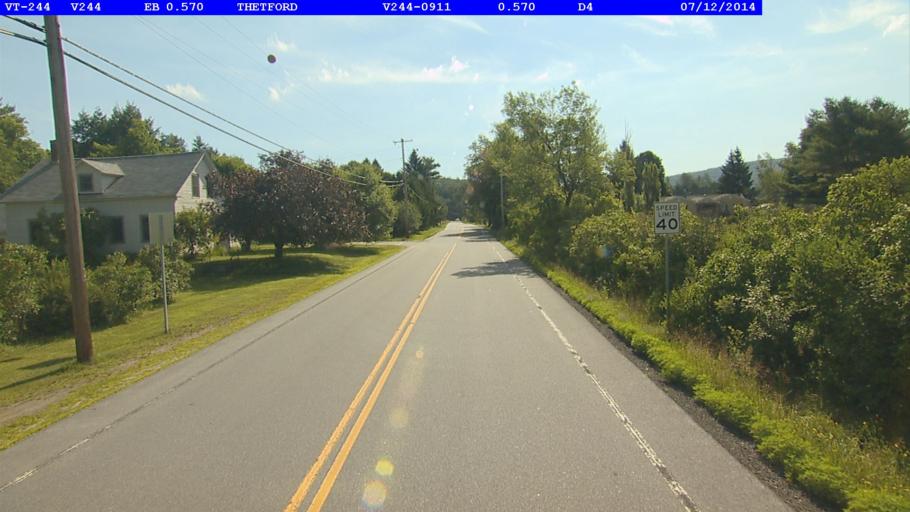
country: US
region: New Hampshire
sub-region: Grafton County
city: Orford
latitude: 43.8874
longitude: -72.2495
